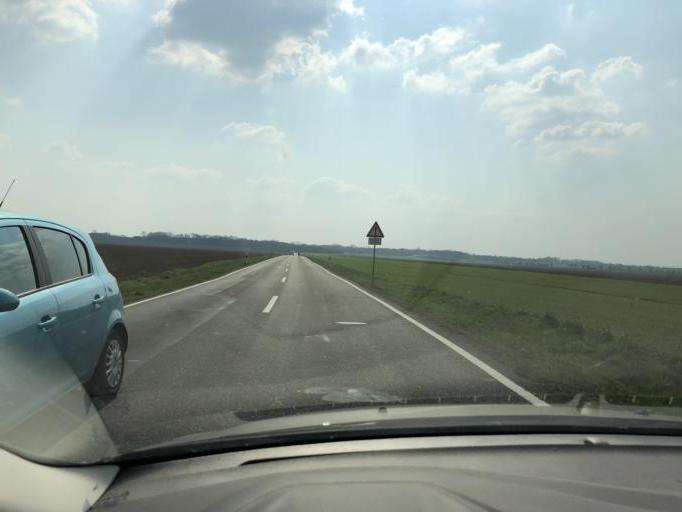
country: DE
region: Saxony-Anhalt
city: Niemberg
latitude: 51.5839
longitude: 12.0698
